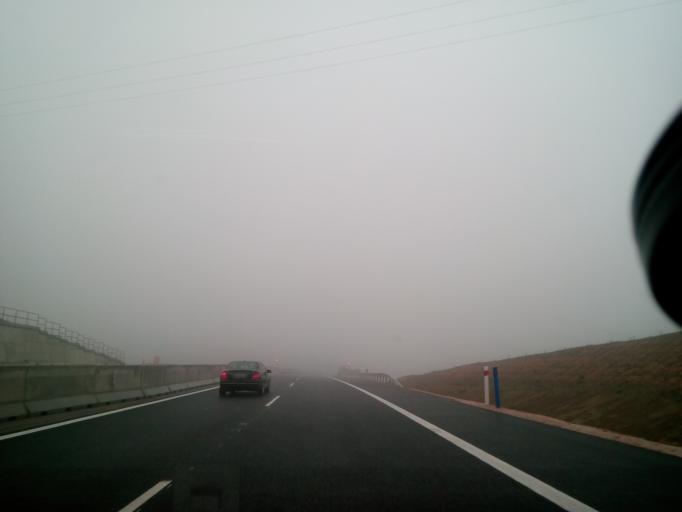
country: SK
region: Presovsky
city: Lipany
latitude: 49.0233
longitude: 20.9889
